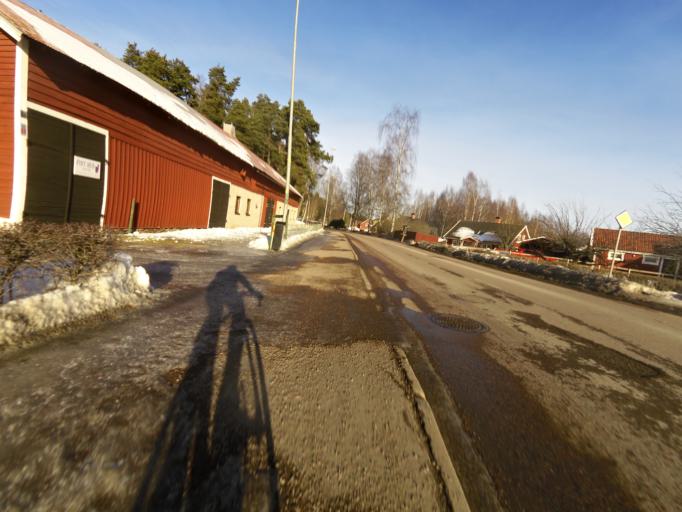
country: SE
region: Gaevleborg
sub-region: Gavle Kommun
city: Valbo
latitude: 60.6575
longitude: 17.0518
